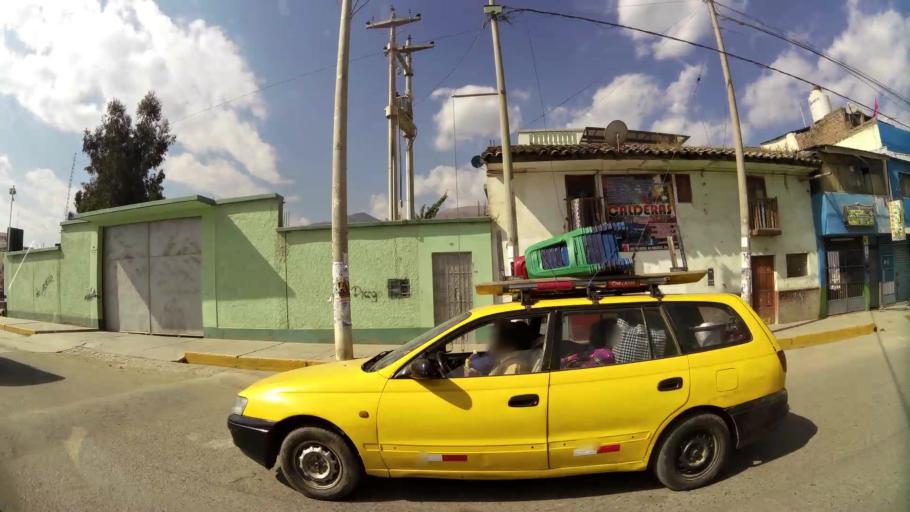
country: PE
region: Junin
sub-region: Provincia de Huancayo
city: Huancayo
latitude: -12.0881
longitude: -75.1981
